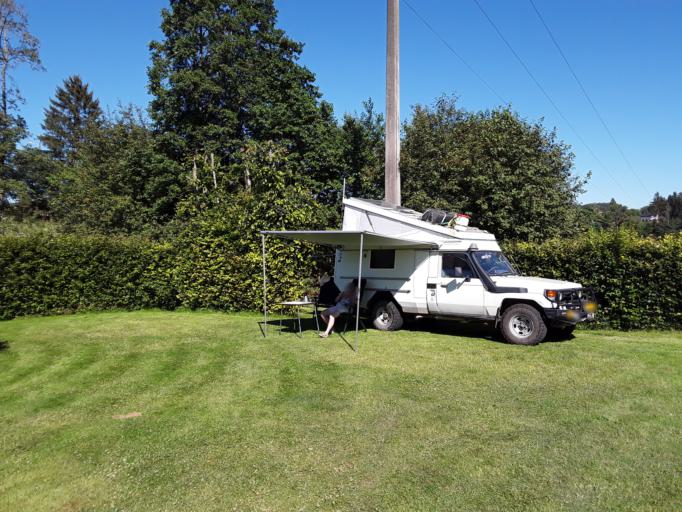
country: BE
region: Wallonia
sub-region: Province de Liege
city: Saint-Vith
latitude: 50.2658
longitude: 6.1406
